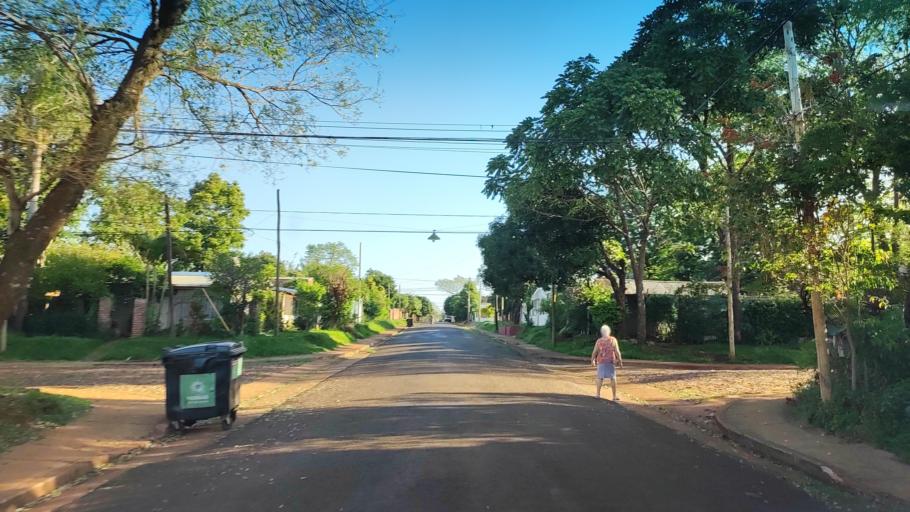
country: AR
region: Misiones
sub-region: Departamento de Capital
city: Posadas
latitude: -27.3707
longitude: -55.9446
